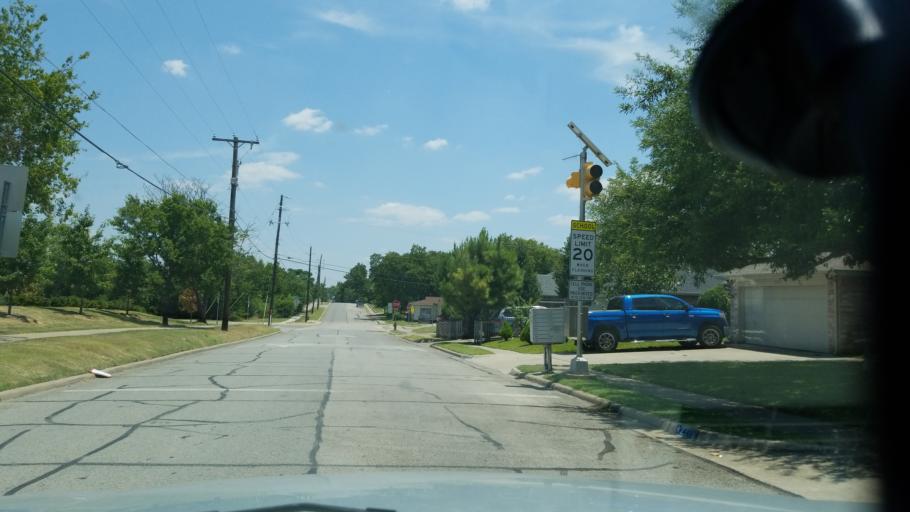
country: US
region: Texas
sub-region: Dallas County
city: Grand Prairie
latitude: 32.7557
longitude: -96.9716
